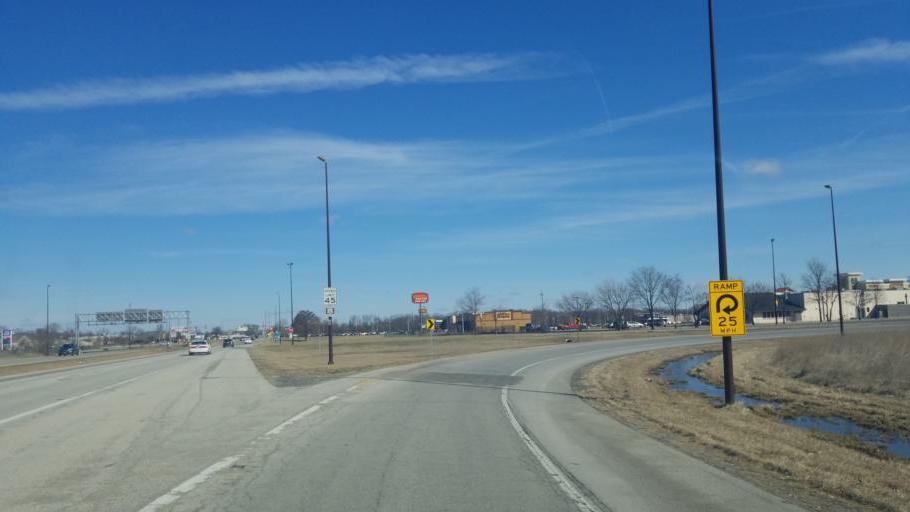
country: US
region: Illinois
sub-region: Sangamon County
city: Southern View
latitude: 39.7438
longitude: -89.6442
